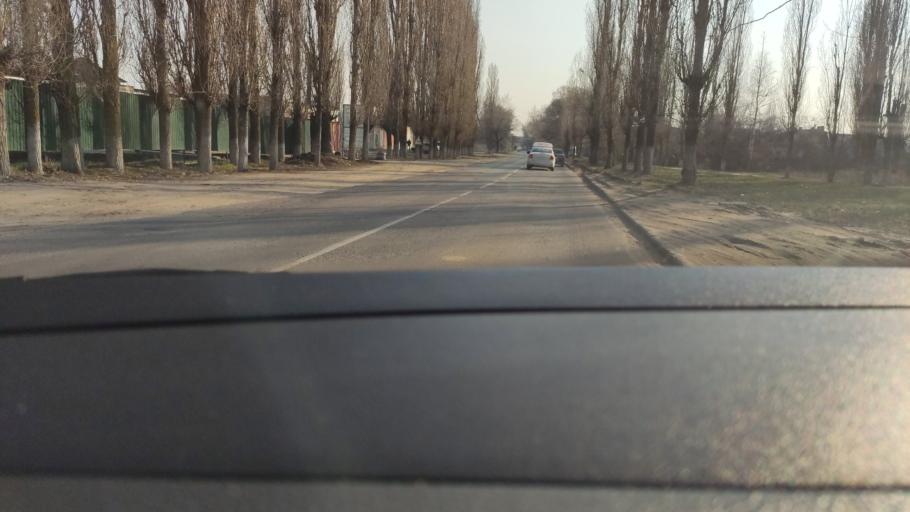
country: RU
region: Voronezj
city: Maslovka
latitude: 51.5842
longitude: 39.3192
